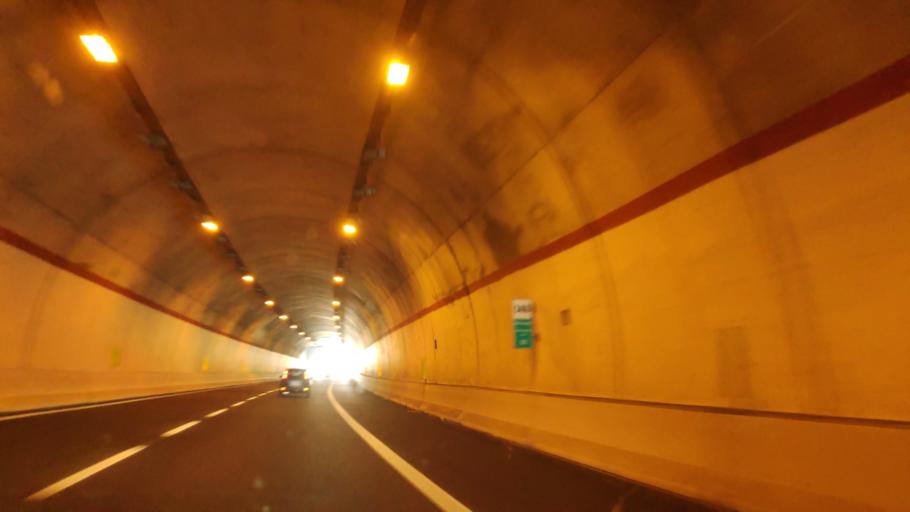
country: IT
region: Basilicate
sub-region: Provincia di Potenza
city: Lauria
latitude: 40.0223
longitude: 15.8796
